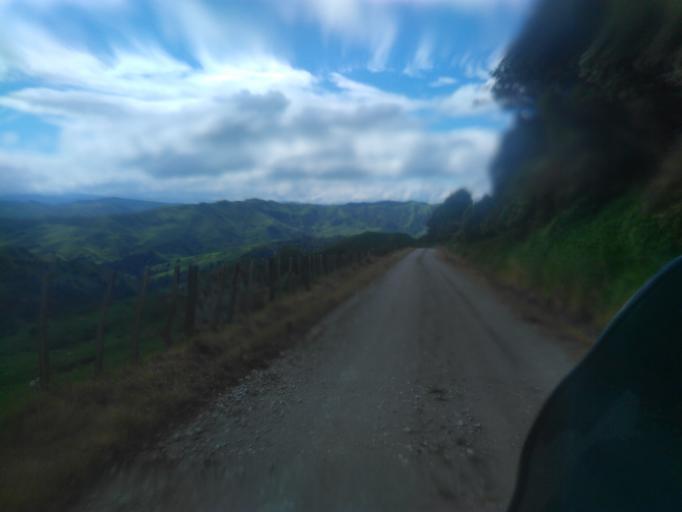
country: NZ
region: Hawke's Bay
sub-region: Wairoa District
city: Wairoa
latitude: -38.7694
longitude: 177.6397
